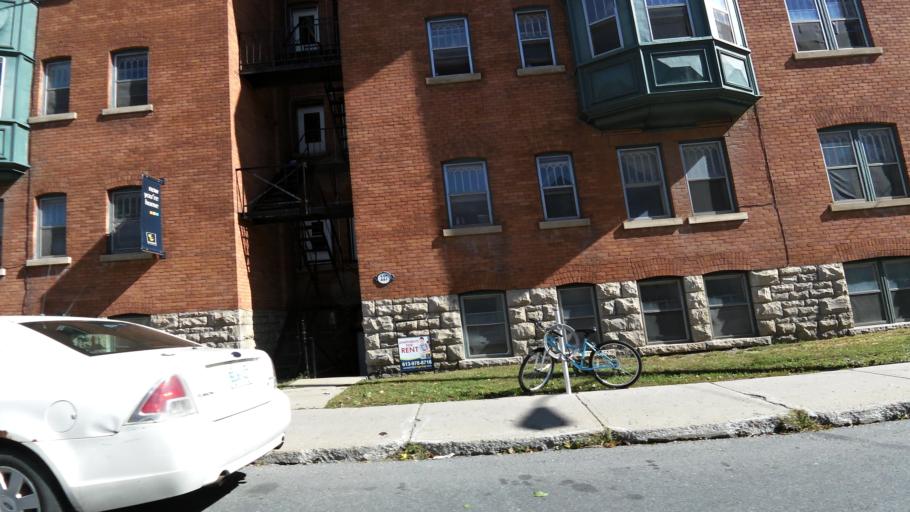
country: CA
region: Ontario
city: Ottawa
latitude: 45.4312
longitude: -75.6750
